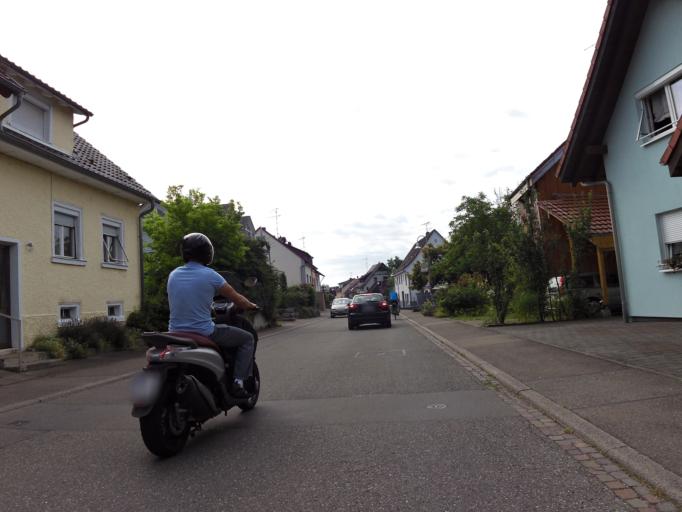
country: DE
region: Baden-Wuerttemberg
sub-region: Freiburg Region
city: Allensbach
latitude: 47.7183
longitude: 9.0631
